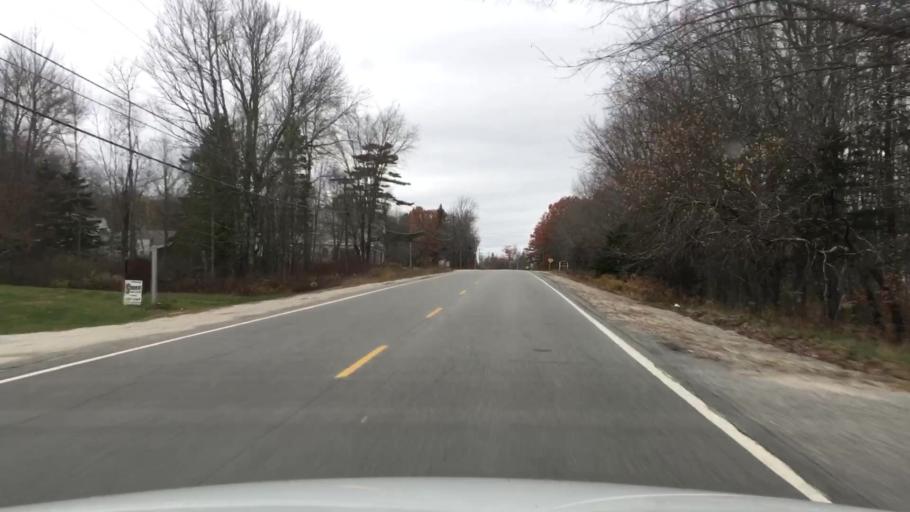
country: US
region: Maine
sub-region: Hancock County
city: Sedgwick
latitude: 44.3999
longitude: -68.5897
